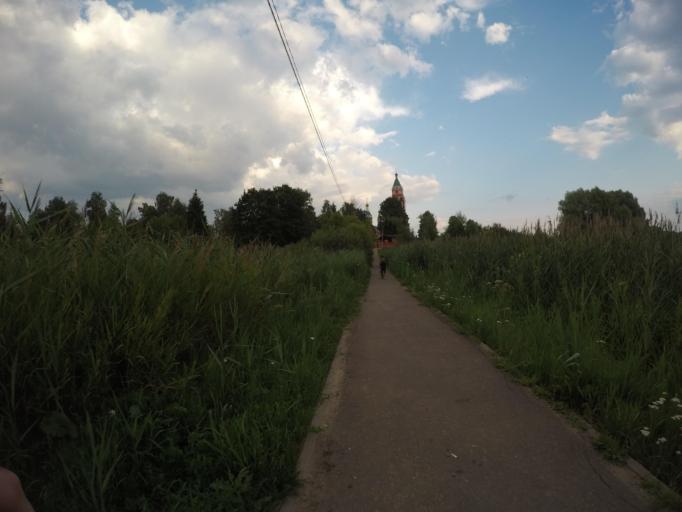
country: RU
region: Moskovskaya
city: Rechitsy
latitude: 55.6016
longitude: 38.5095
